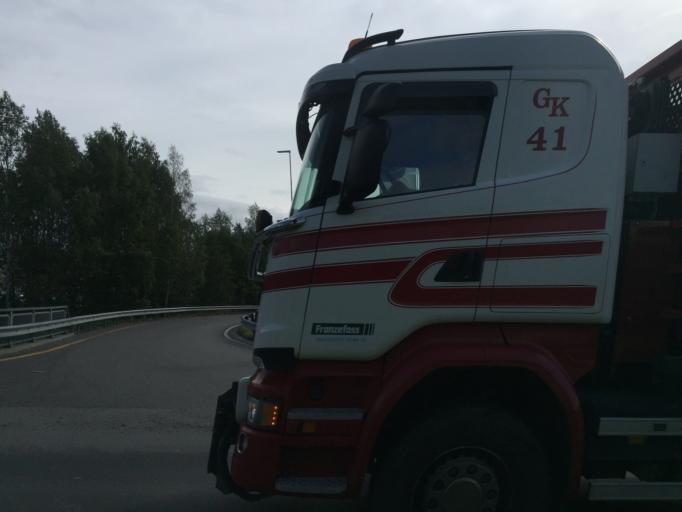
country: NO
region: Akershus
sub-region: Lorenskog
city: Kjenn
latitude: 59.9300
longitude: 10.9466
